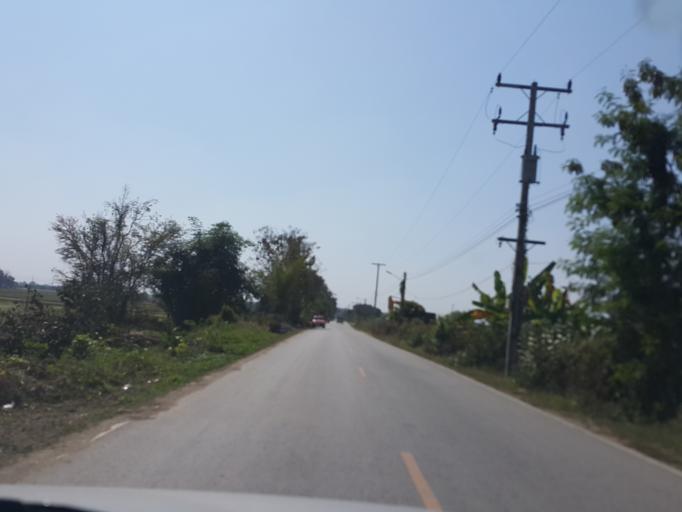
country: TH
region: Chiang Mai
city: San Kamphaeng
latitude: 18.7377
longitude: 99.0972
